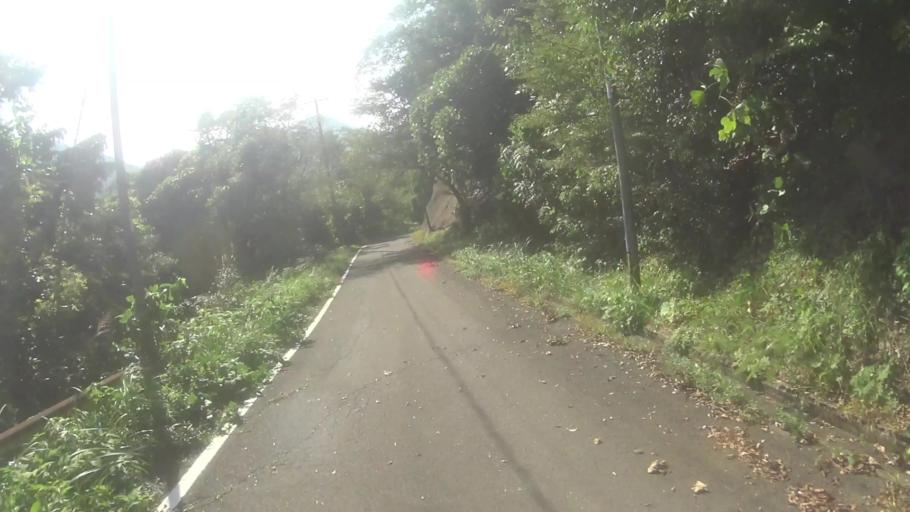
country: JP
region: Kyoto
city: Miyazu
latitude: 35.6983
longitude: 135.1586
